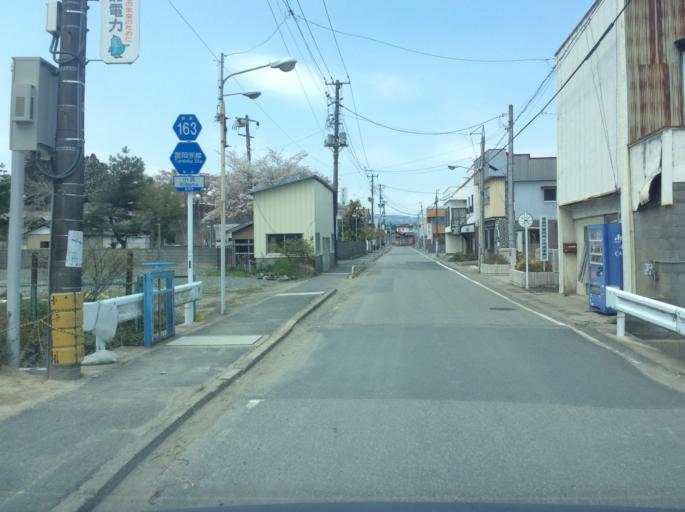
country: JP
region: Fukushima
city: Namie
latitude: 37.3360
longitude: 141.0201
